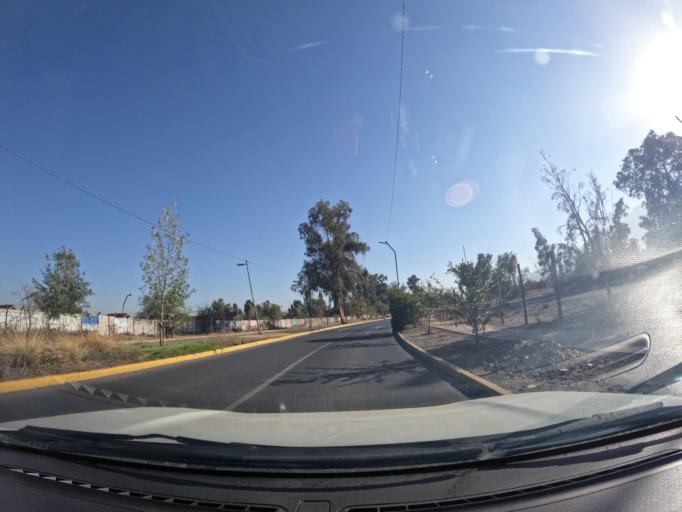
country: CL
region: Santiago Metropolitan
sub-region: Provincia de Santiago
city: Villa Presidente Frei, Nunoa, Santiago, Chile
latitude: -33.5043
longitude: -70.5439
